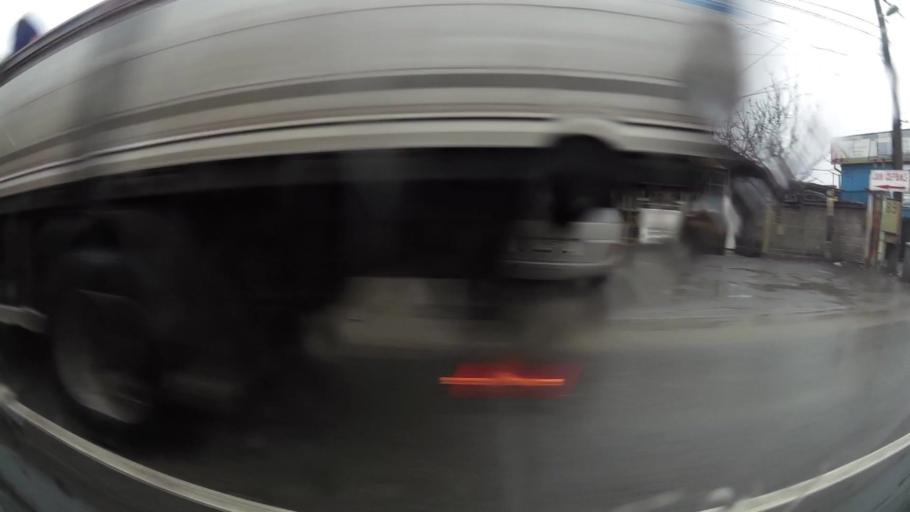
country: BG
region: Sofia-Capital
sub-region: Stolichna Obshtina
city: Sofia
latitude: 42.6357
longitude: 23.3537
